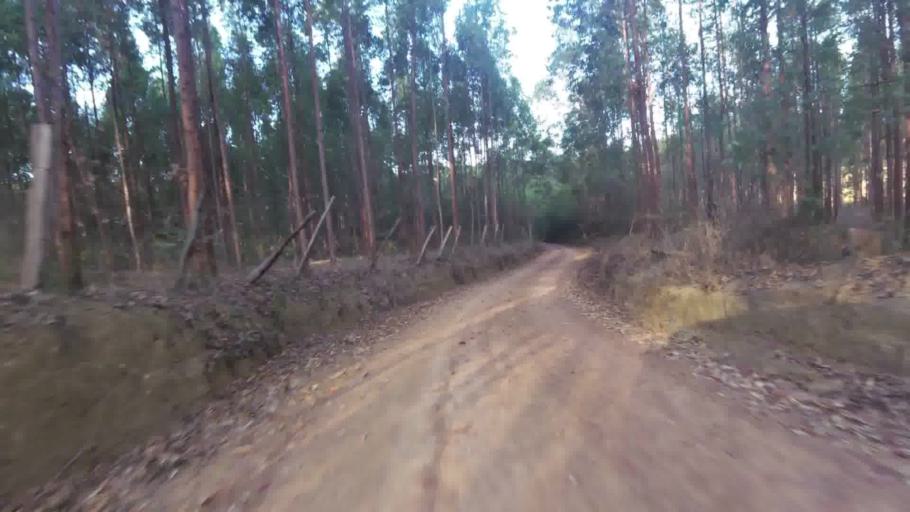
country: BR
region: Espirito Santo
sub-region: Marataizes
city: Marataizes
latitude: -21.1626
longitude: -41.0398
